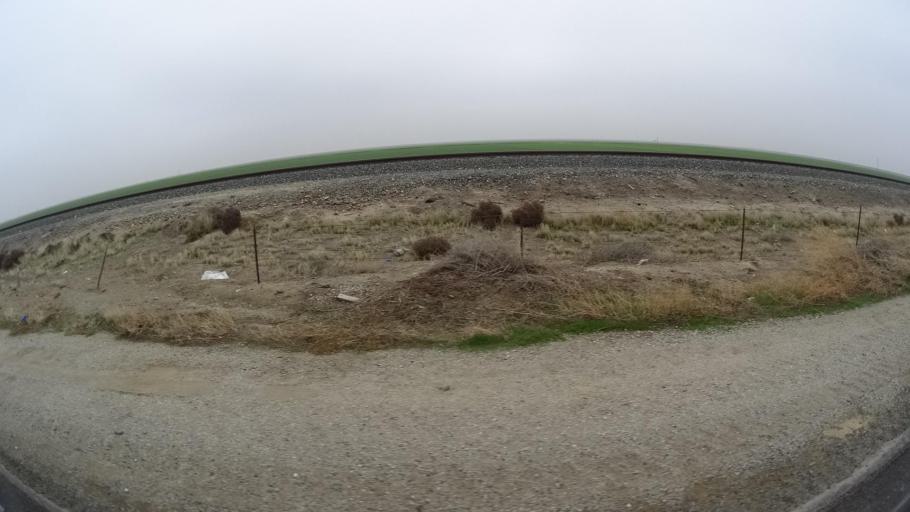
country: US
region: California
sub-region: Kern County
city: Greenfield
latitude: 35.1800
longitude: -119.1375
